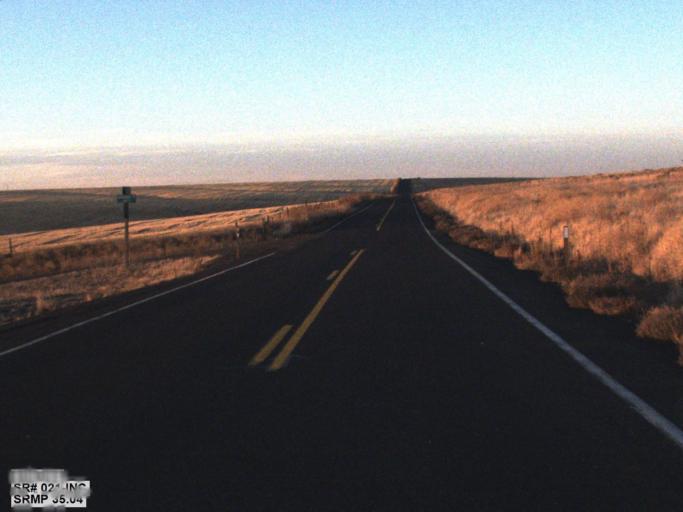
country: US
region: Washington
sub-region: Adams County
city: Ritzville
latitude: 47.0577
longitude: -118.6630
